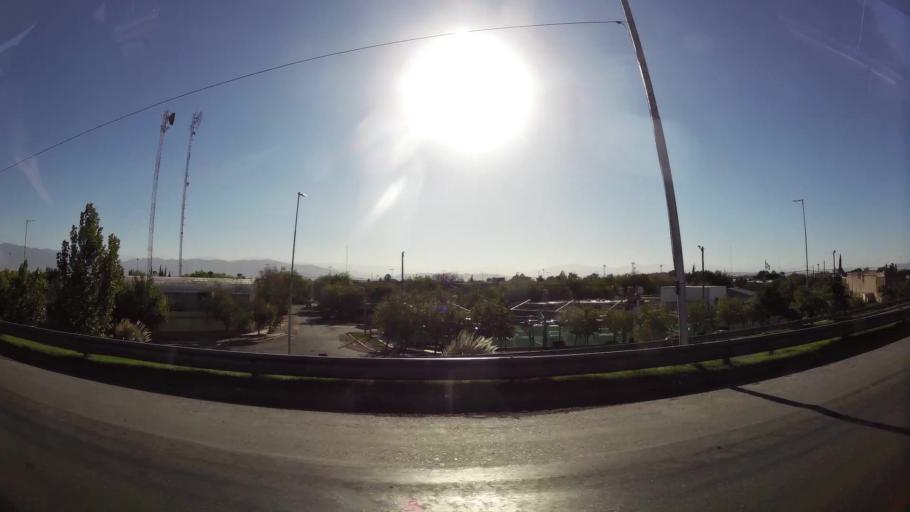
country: AR
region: San Juan
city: Villa Krause
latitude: -31.5573
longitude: -68.5139
